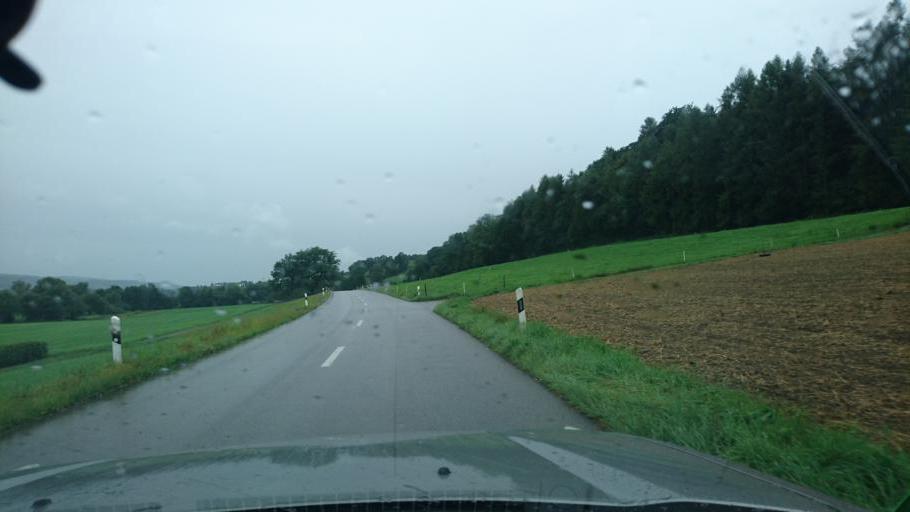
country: CH
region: Zurich
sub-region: Bezirk Uster
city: Uster / Nossikon
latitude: 47.3296
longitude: 8.7314
